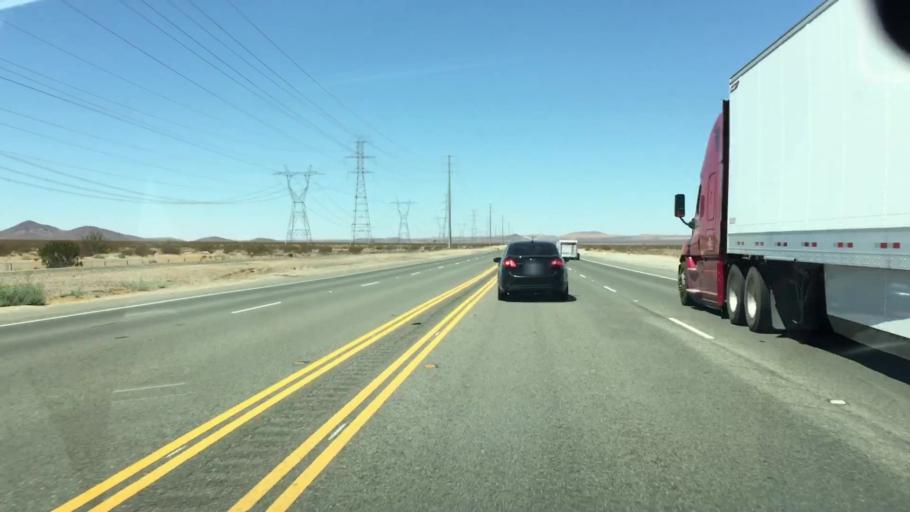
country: US
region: California
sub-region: San Bernardino County
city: Adelanto
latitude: 34.7651
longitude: -117.4755
